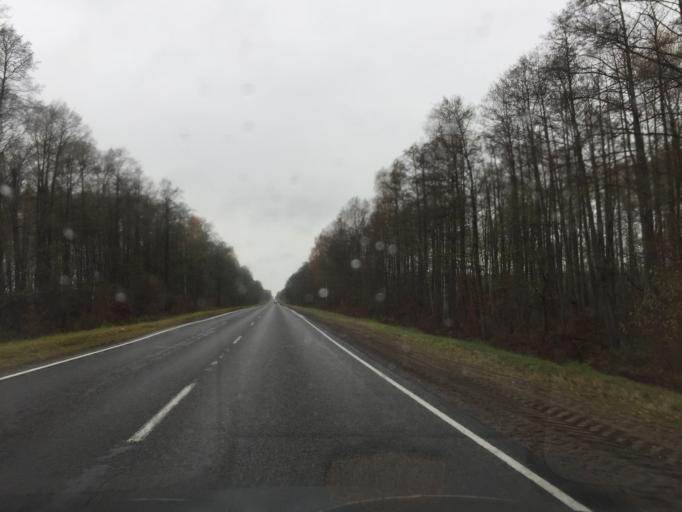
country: BY
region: Mogilev
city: Slawharad
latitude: 53.3555
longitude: 30.8319
